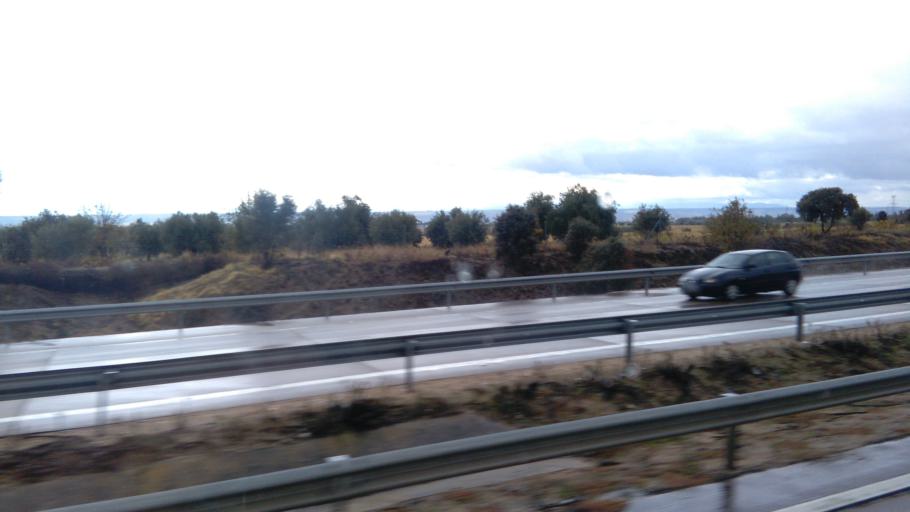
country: ES
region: Castille-La Mancha
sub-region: Province of Toledo
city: Cervera de los Montes
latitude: 40.0192
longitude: -4.8011
